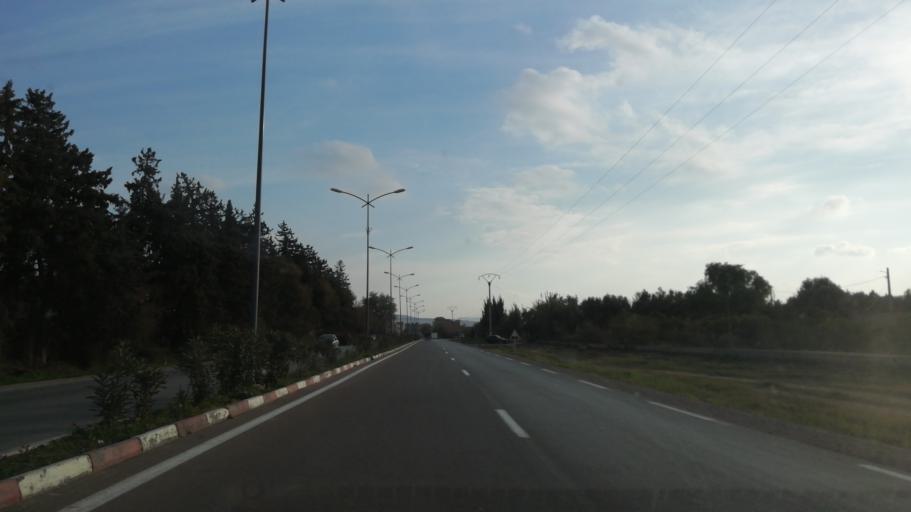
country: DZ
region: Mascara
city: Mascara
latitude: 35.6019
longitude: 0.0637
